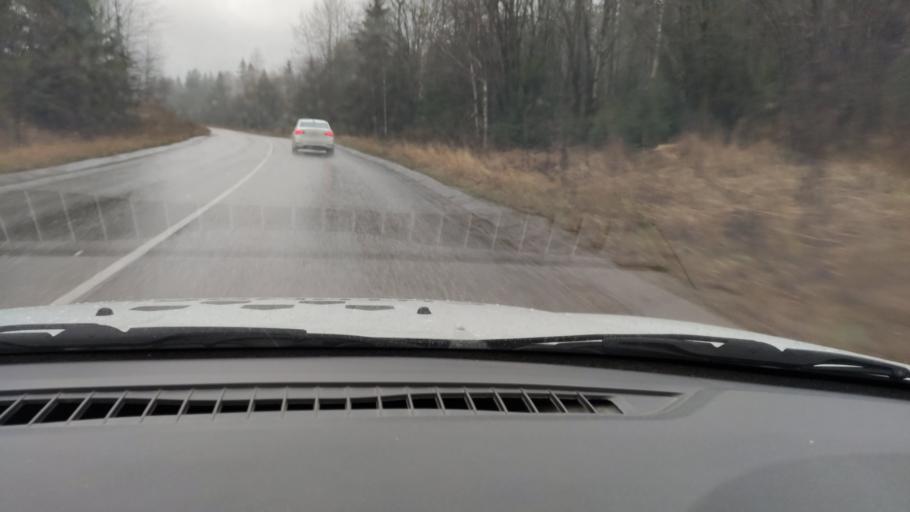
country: RU
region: Perm
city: Novyye Lyady
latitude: 58.0371
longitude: 56.6003
